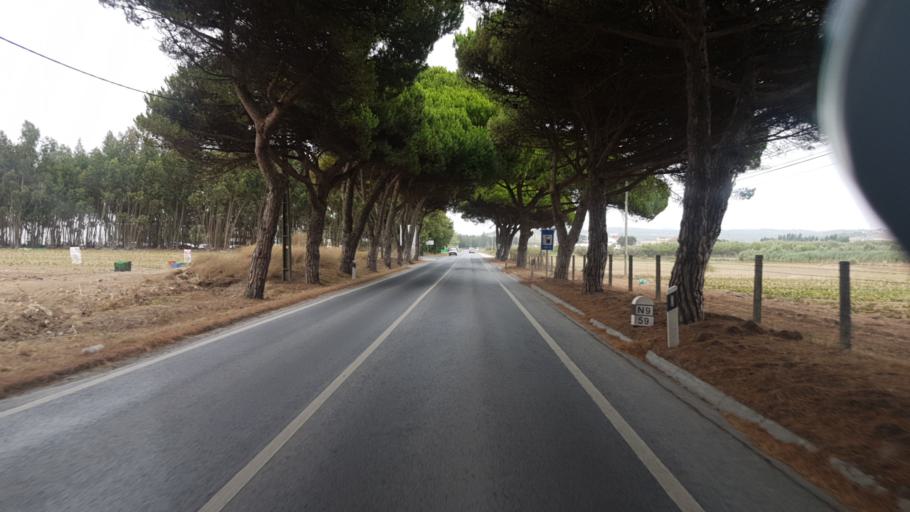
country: PT
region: Lisbon
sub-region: Torres Vedras
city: Silveira
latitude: 39.0923
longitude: -9.3422
